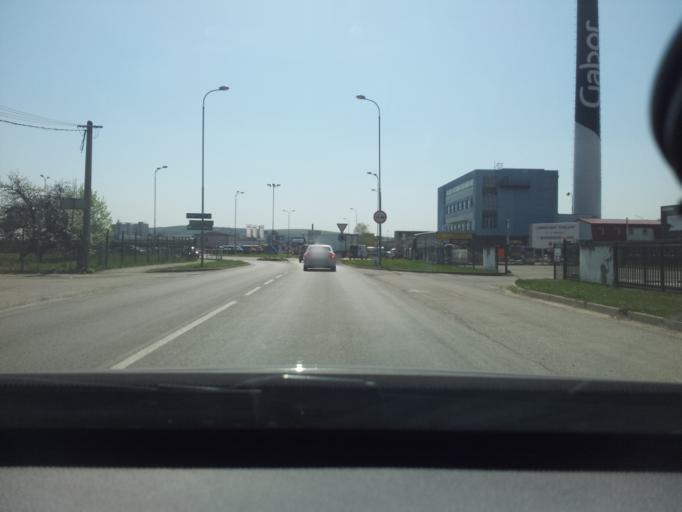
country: SK
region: Nitriansky
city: Banovce nad Bebravou
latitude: 48.7314
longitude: 18.2439
